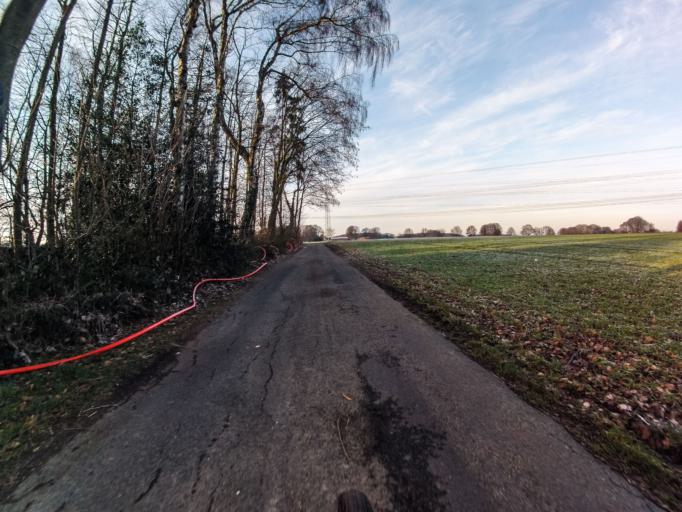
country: DE
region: North Rhine-Westphalia
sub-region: Regierungsbezirk Munster
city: Mettingen
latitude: 52.2803
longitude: 7.8100
